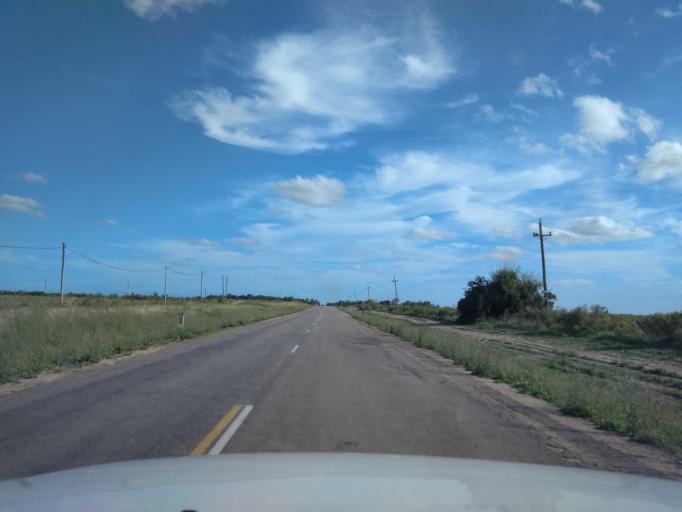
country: UY
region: Canelones
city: San Ramon
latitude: -34.2308
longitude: -55.9287
